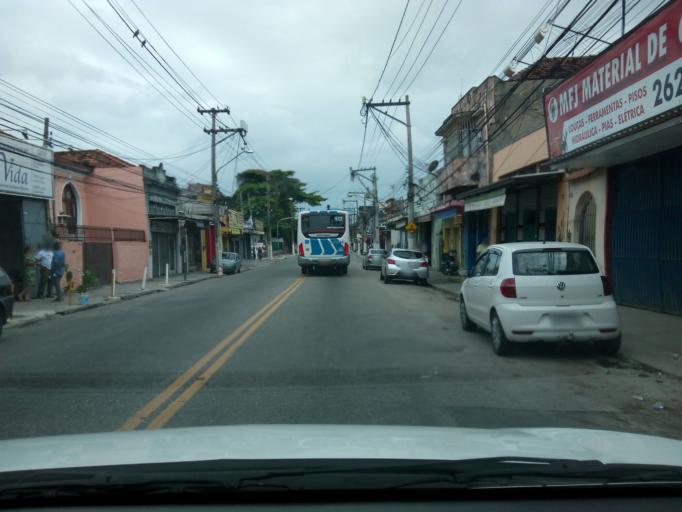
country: BR
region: Rio de Janeiro
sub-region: Niteroi
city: Niteroi
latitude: -22.8708
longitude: -43.1047
